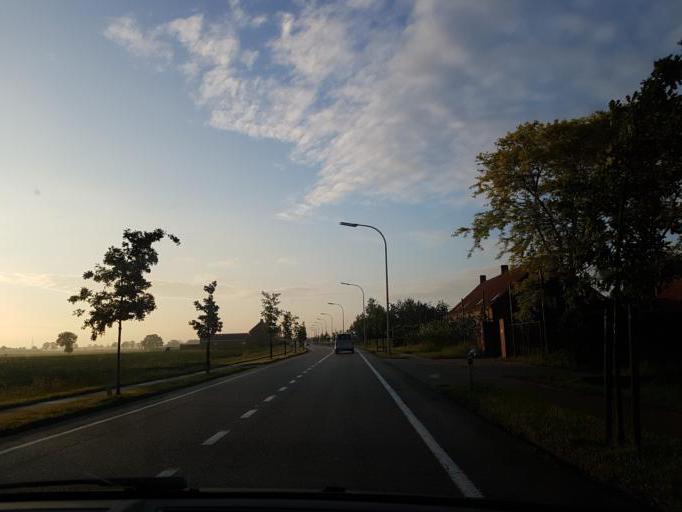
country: BE
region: Flanders
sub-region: Provincie Antwerpen
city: Hoogstraten
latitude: 51.3959
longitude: 4.6978
